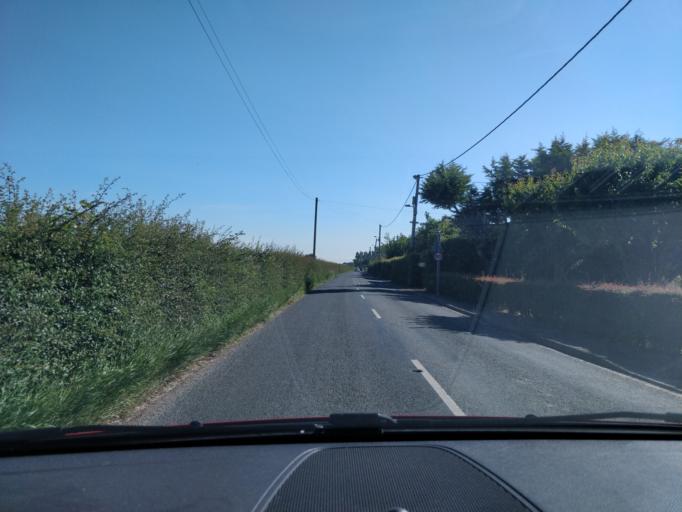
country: GB
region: England
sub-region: Lancashire
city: Banks
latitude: 53.6979
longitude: -2.8862
